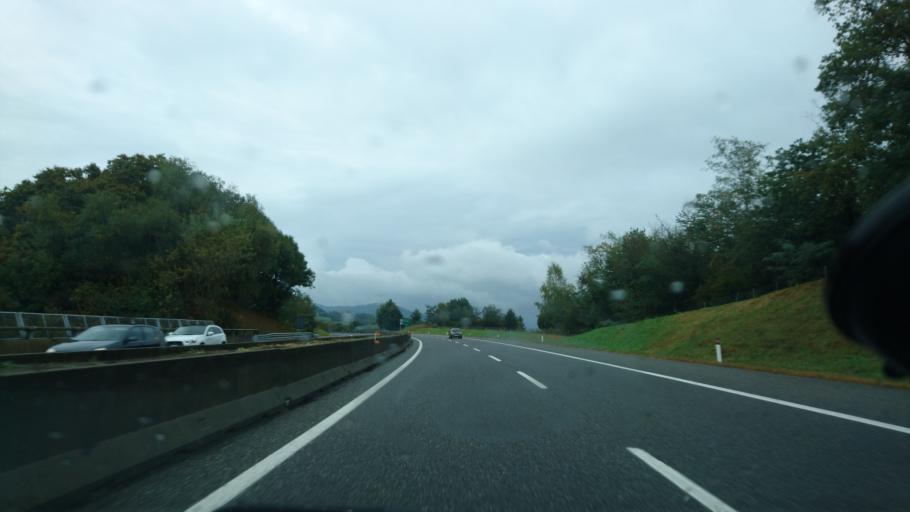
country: IT
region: Piedmont
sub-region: Provincia di Novara
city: Pisano
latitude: 45.7955
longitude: 8.5257
